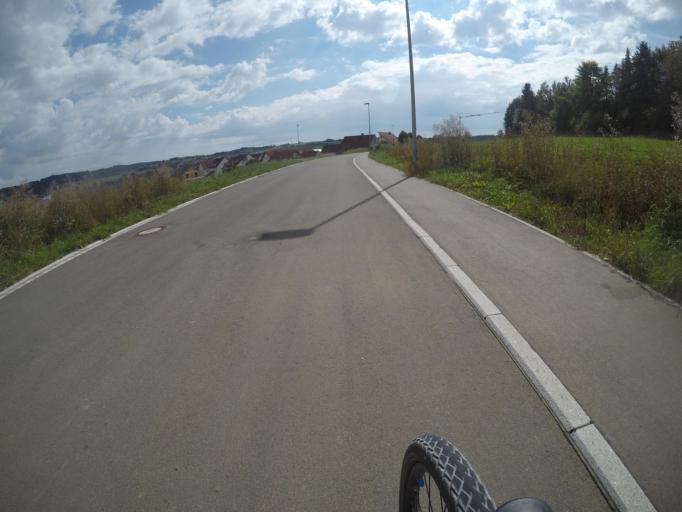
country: DE
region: Baden-Wuerttemberg
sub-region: Tuebingen Region
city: Munsingen
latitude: 48.4197
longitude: 9.4981
